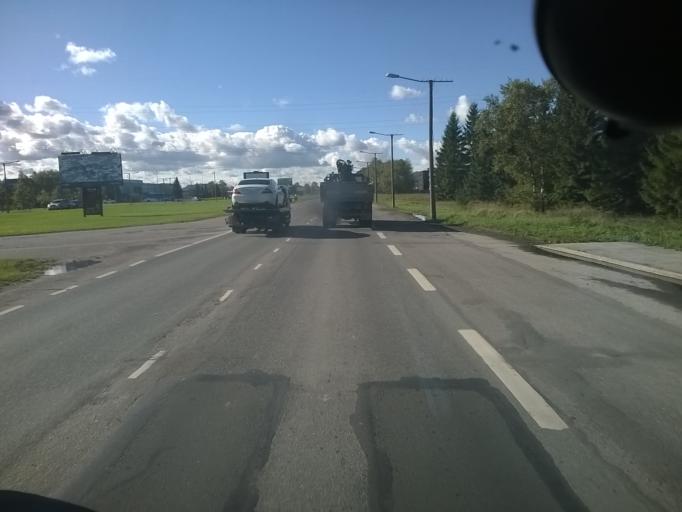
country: EE
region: Harju
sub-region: Tallinna linn
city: Kose
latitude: 59.4353
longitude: 24.8685
